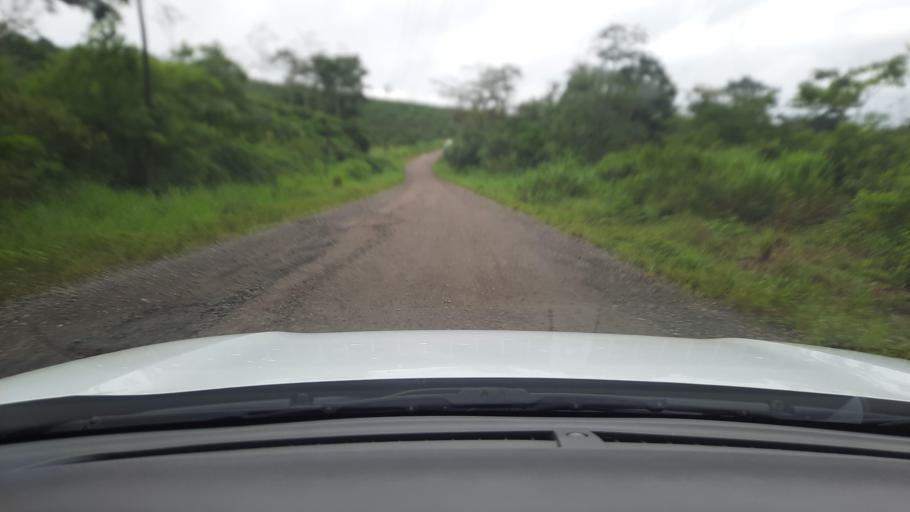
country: CR
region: Alajuela
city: San Jose
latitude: 10.9990
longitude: -85.2844
